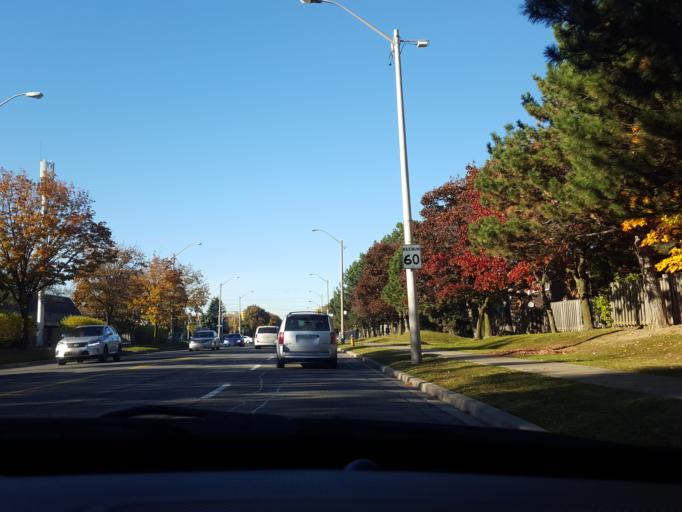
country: CA
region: Ontario
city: Scarborough
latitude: 43.8099
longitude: -79.2792
